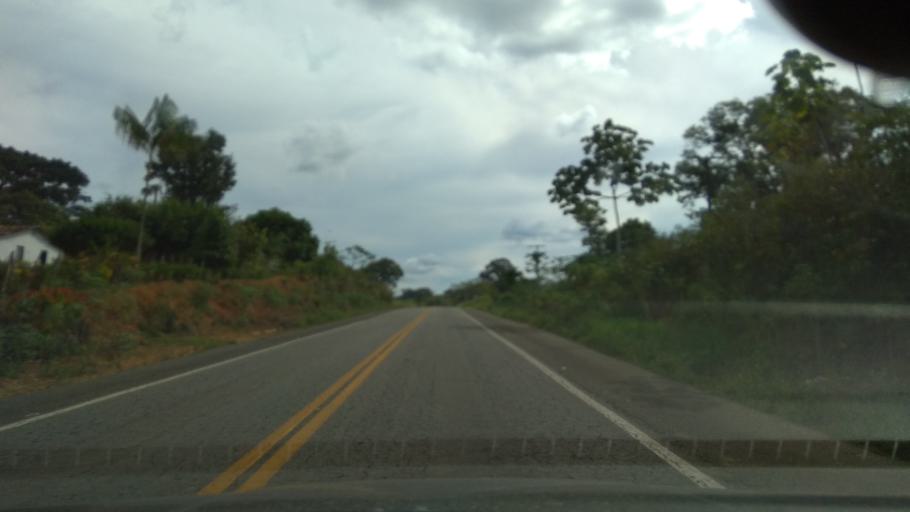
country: BR
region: Bahia
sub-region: Ubata
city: Ubata
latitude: -14.2291
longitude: -39.4428
